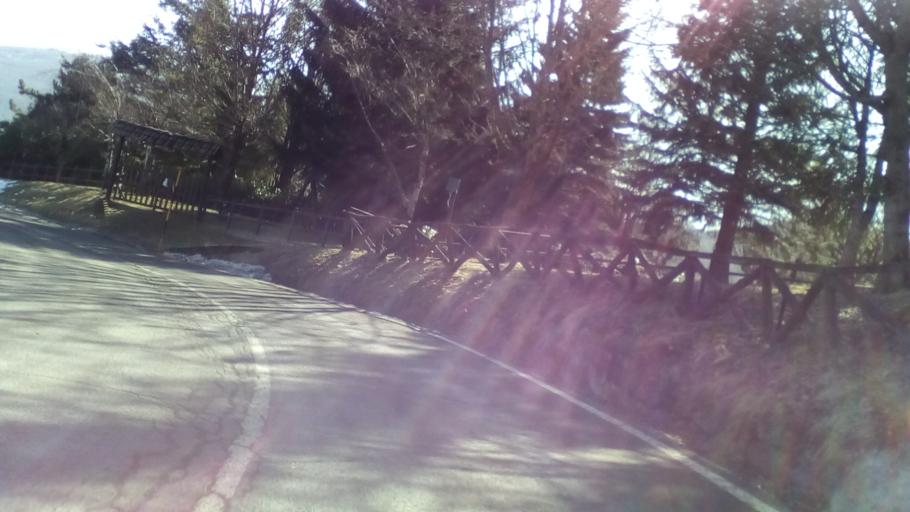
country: IT
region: Emilia-Romagna
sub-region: Provincia di Modena
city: Pievepelago
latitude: 44.1939
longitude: 10.5462
